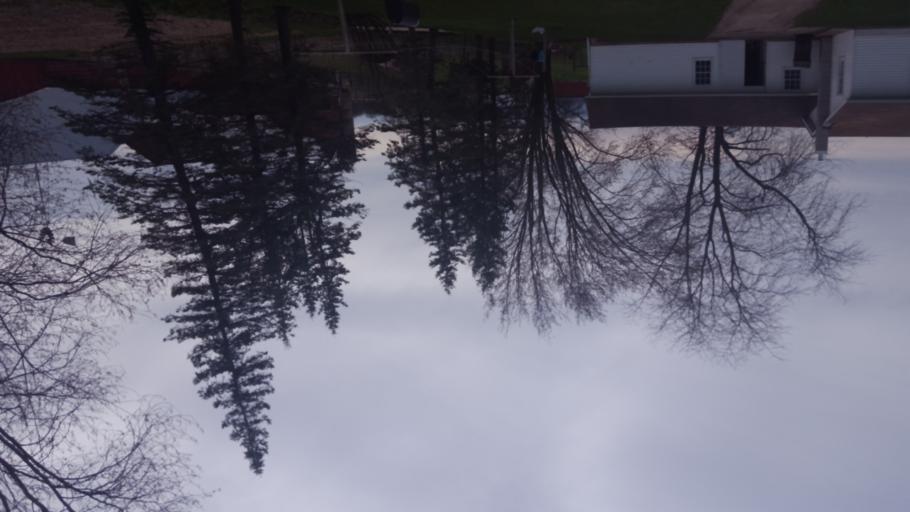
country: US
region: Michigan
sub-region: Clare County
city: Clare
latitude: 43.8732
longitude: -84.6947
